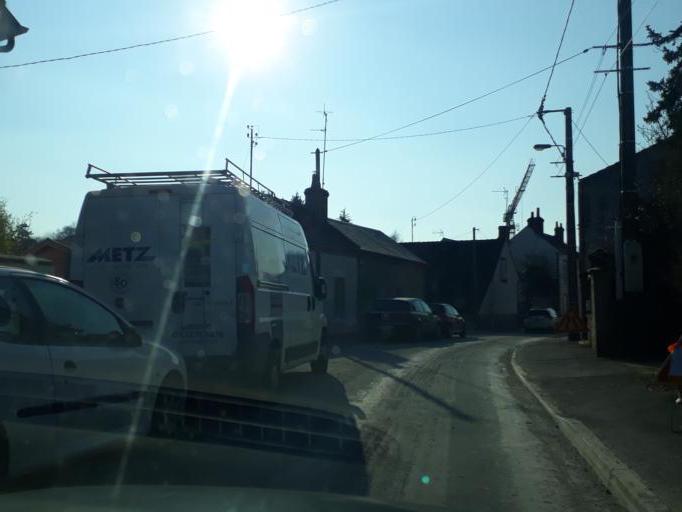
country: FR
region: Centre
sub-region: Departement du Loiret
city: Saint-Jean-le-Blanc
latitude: 47.9051
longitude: 1.9385
